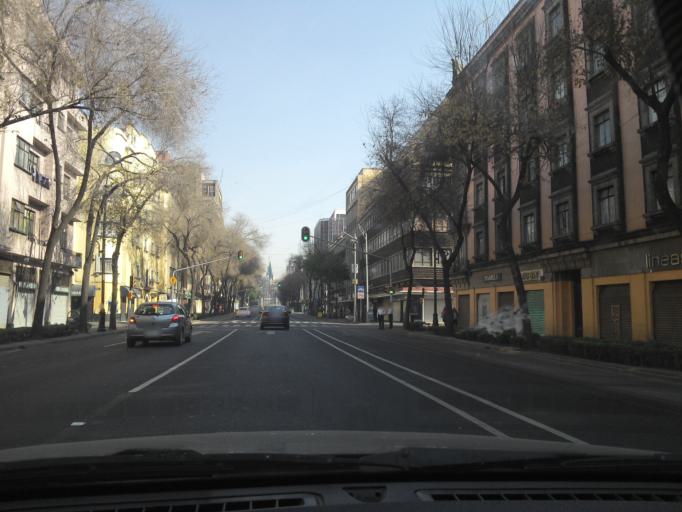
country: MX
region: Mexico City
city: Mexico City
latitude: 19.4279
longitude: -99.1341
